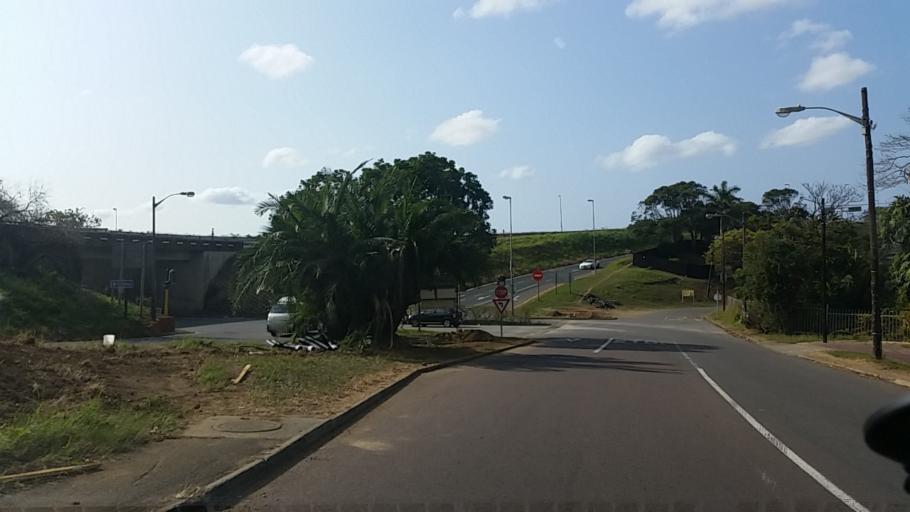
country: ZA
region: KwaZulu-Natal
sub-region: eThekwini Metropolitan Municipality
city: Berea
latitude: -29.8294
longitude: 30.9571
